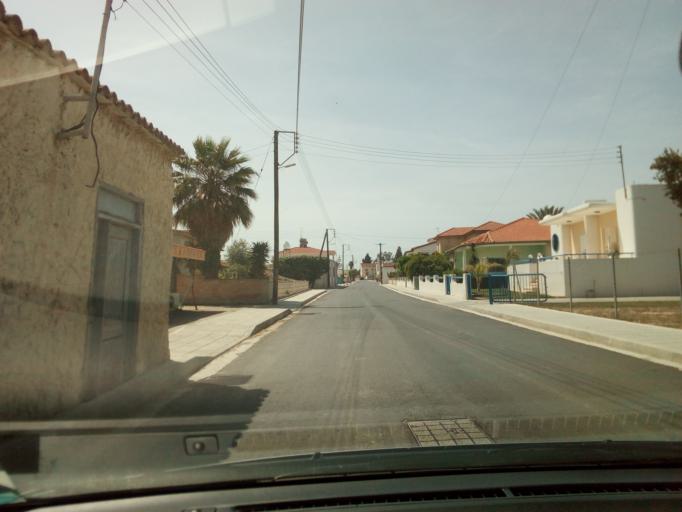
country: CY
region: Larnaka
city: Athienou
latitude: 35.0611
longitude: 33.5391
